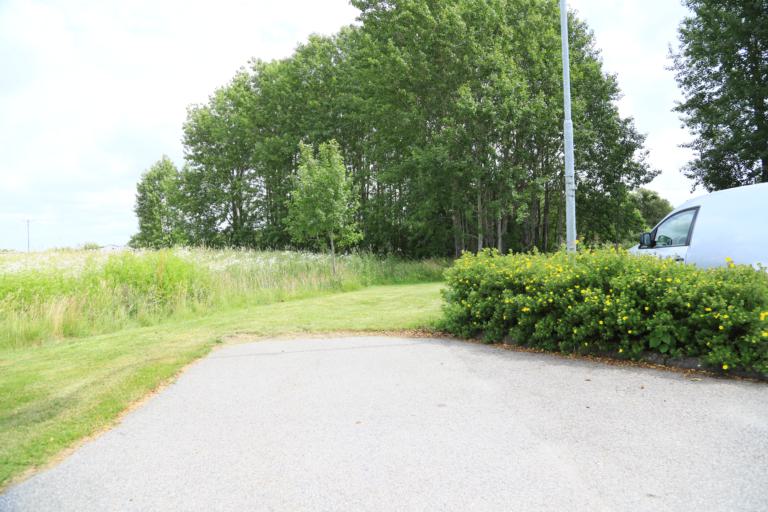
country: SE
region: Halland
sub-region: Varbergs Kommun
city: Traslovslage
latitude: 57.1127
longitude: 12.3031
